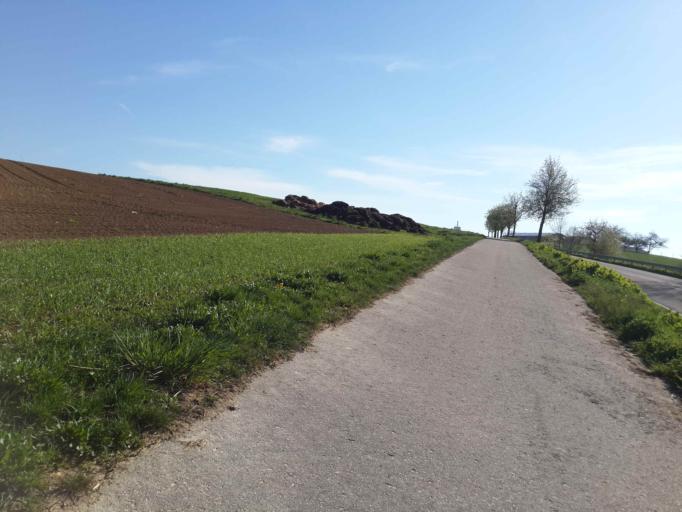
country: DE
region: Baden-Wuerttemberg
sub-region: Regierungsbezirk Stuttgart
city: Schwaigern
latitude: 49.1544
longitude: 9.0624
